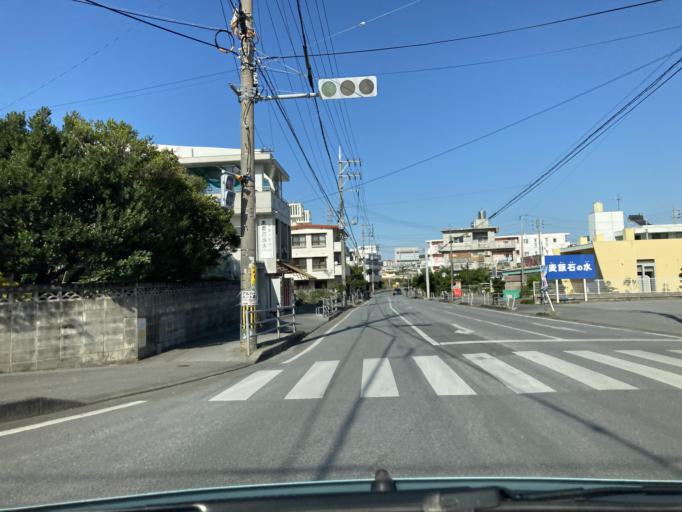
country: JP
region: Okinawa
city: Tomigusuku
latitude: 26.1856
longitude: 127.7078
